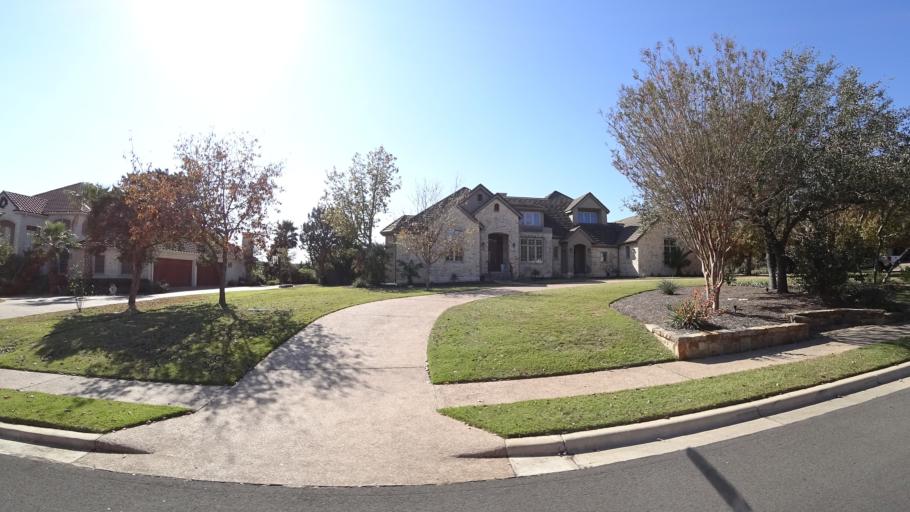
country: US
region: Texas
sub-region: Williamson County
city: Anderson Mill
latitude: 30.3811
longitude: -97.8490
